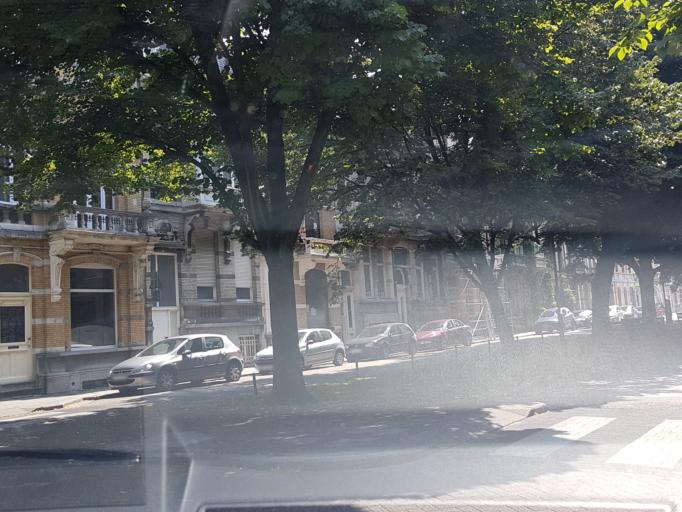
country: BE
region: Flanders
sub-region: Provincie Antwerpen
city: Antwerpen
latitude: 51.1986
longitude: 4.4245
